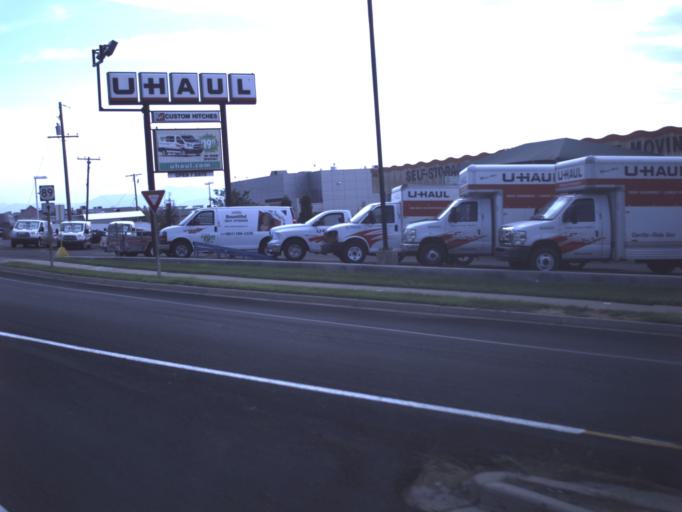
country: US
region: Utah
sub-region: Davis County
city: Woods Cross
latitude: 40.8669
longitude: -111.8924
